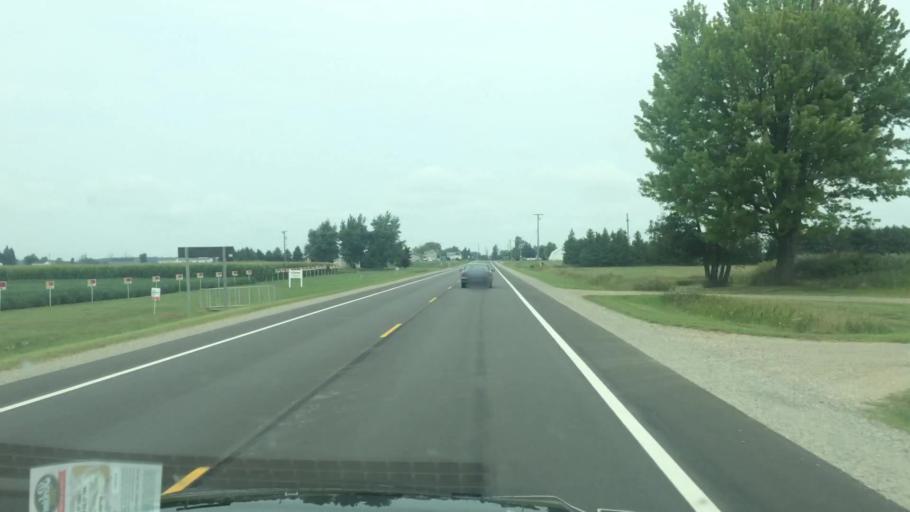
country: US
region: Michigan
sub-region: Huron County
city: Bad Axe
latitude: 43.9983
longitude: -83.0077
